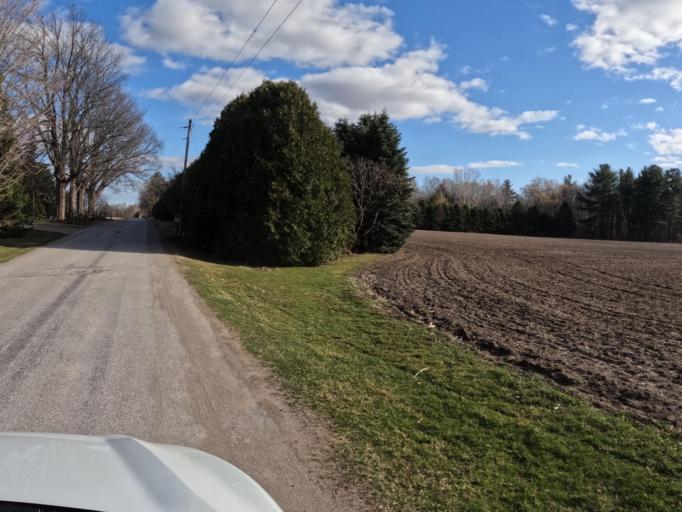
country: CA
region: Ontario
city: Norfolk County
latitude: 42.7782
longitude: -80.5199
